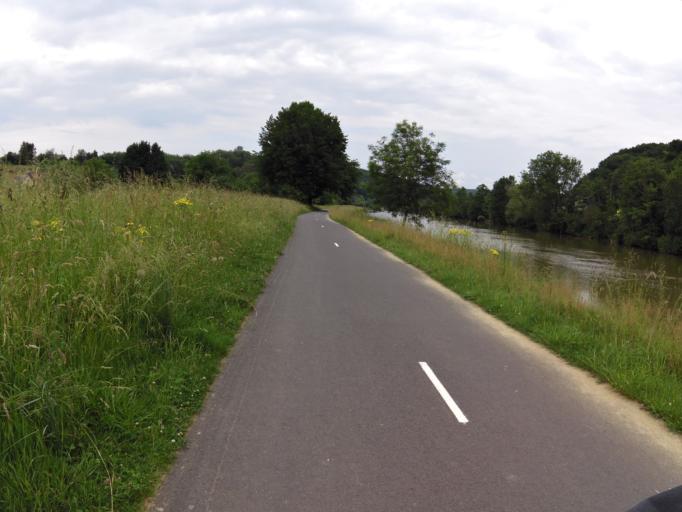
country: FR
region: Champagne-Ardenne
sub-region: Departement des Ardennes
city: Montcy-Notre-Dame
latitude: 49.7741
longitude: 4.7515
